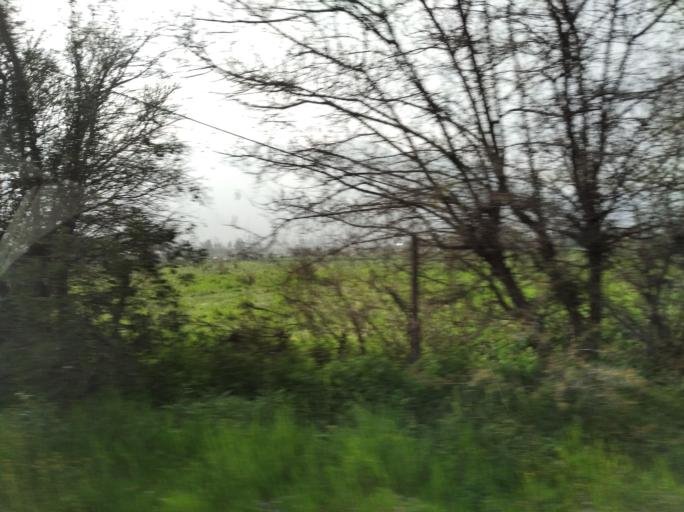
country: CL
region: Santiago Metropolitan
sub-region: Provincia de Chacabuco
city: Lampa
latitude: -33.2376
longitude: -70.9261
